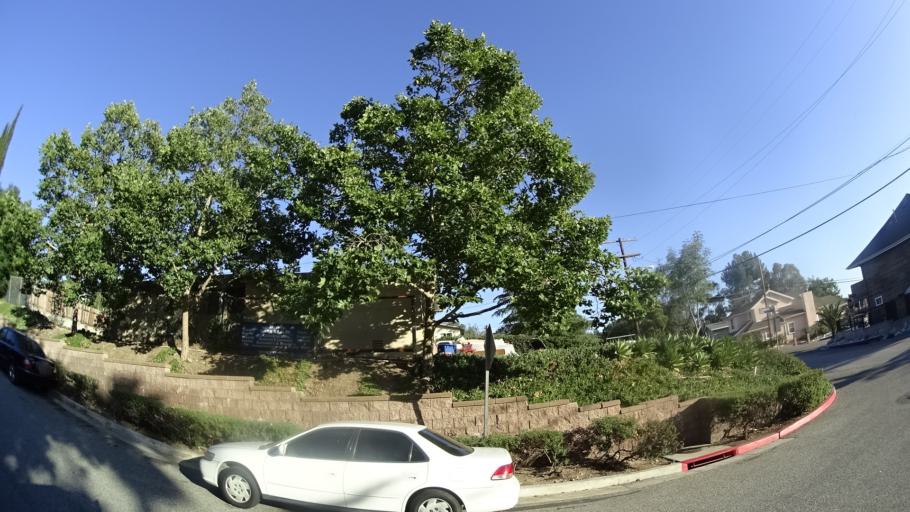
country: US
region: California
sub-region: Los Angeles County
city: La Crescenta-Montrose
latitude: 34.2673
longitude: -118.2958
